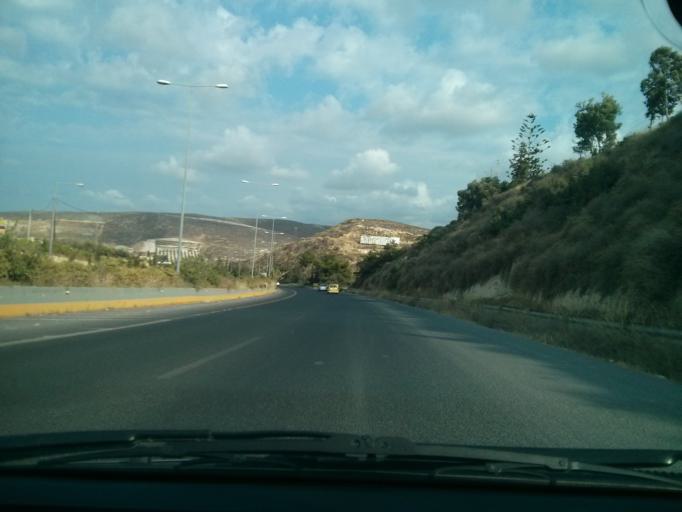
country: GR
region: Crete
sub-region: Nomos Irakleiou
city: Nea Alikarnassos
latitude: 35.3216
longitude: 25.1852
